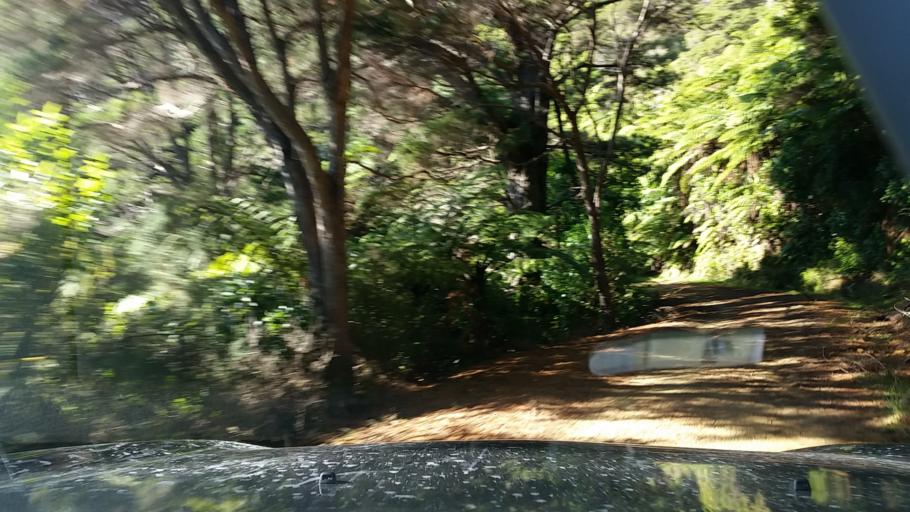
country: NZ
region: Marlborough
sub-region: Marlborough District
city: Picton
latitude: -41.1198
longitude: 173.9923
